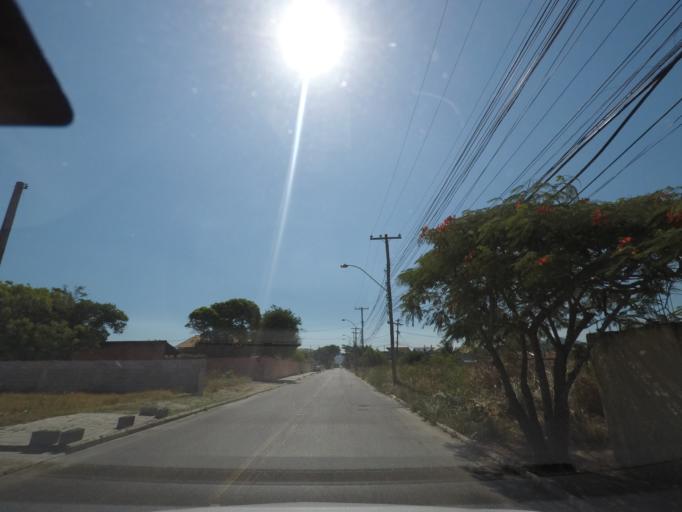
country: BR
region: Rio de Janeiro
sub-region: Marica
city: Marica
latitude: -22.9671
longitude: -42.9444
